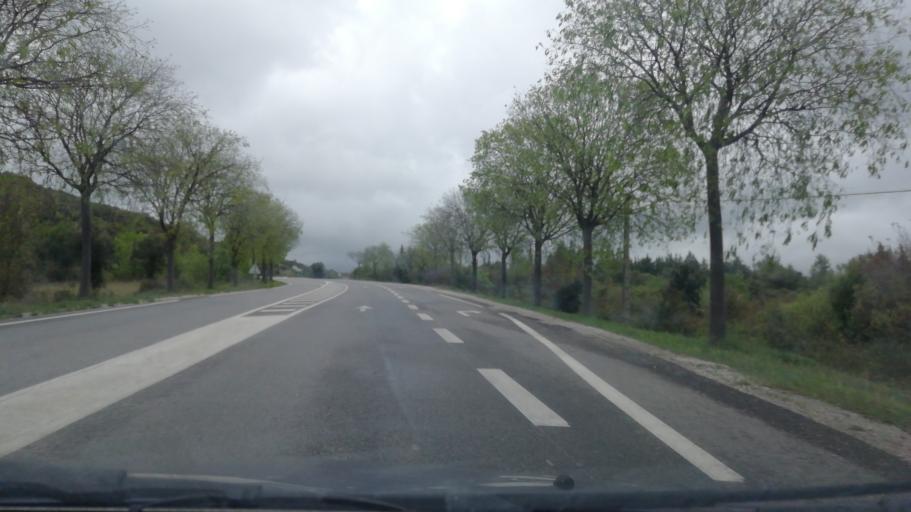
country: FR
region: Languedoc-Roussillon
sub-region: Departement de l'Herault
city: Les Matelles
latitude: 43.7221
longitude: 3.7950
